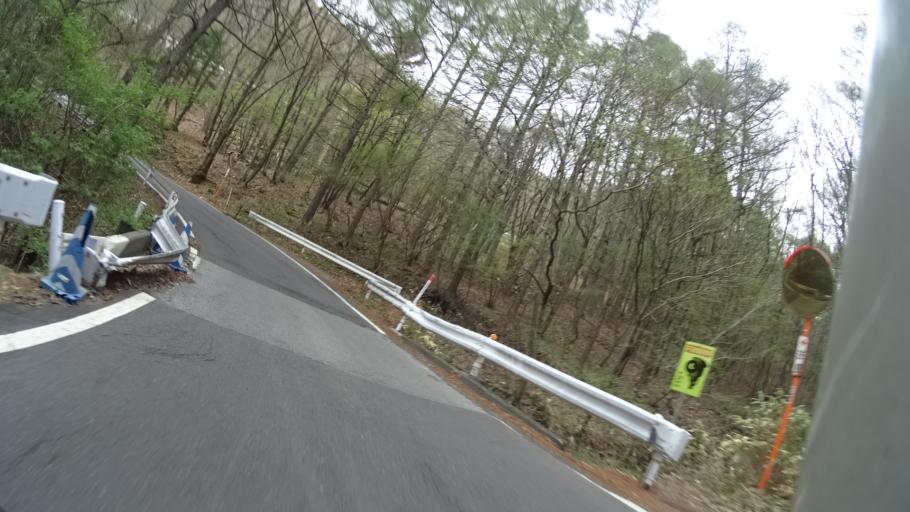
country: JP
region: Nagano
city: Suwa
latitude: 36.1364
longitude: 138.1325
